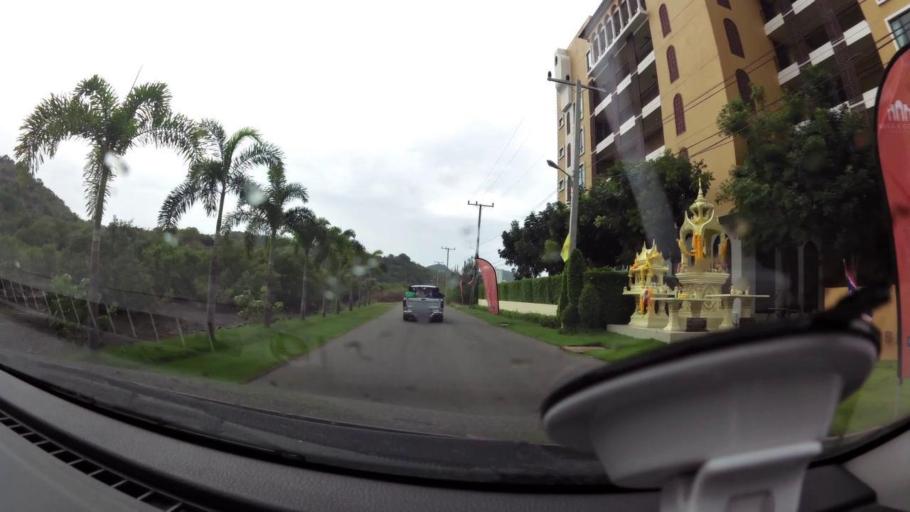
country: TH
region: Prachuap Khiri Khan
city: Pran Buri
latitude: 12.4200
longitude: 99.9802
